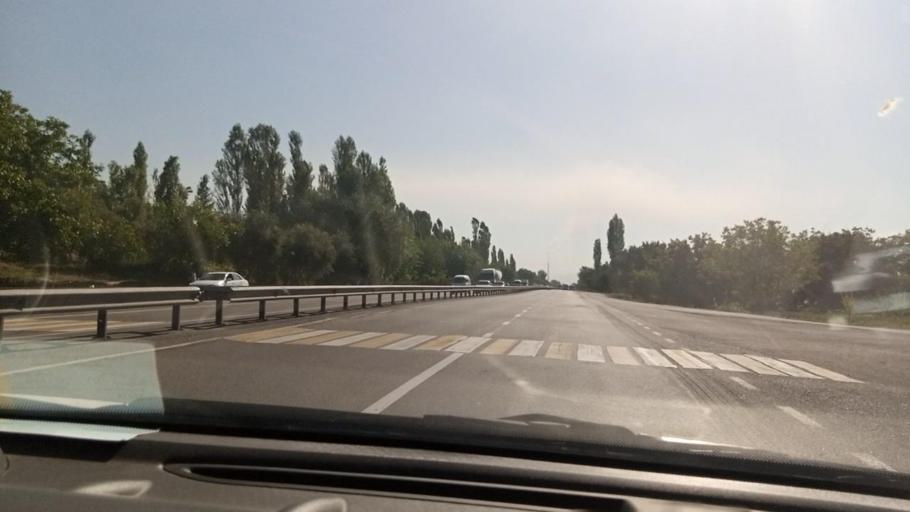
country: UZ
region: Toshkent
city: Ohangaron
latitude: 40.8997
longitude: 69.6981
